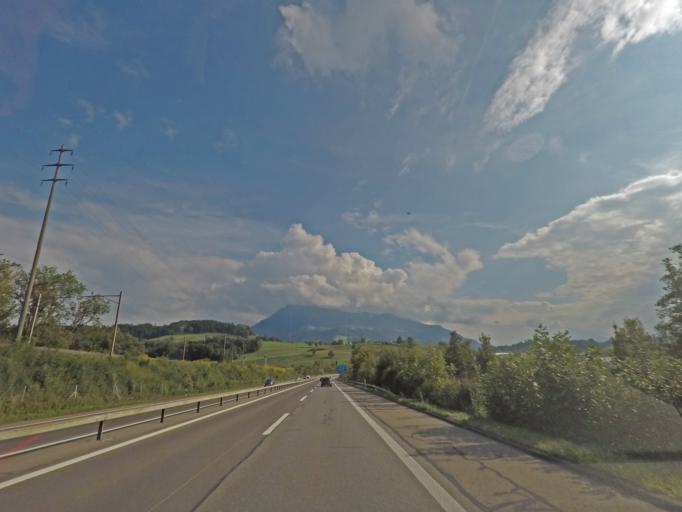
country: CH
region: Lucerne
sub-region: Lucerne-Land District
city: Meierskappel
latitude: 47.1168
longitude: 8.4535
